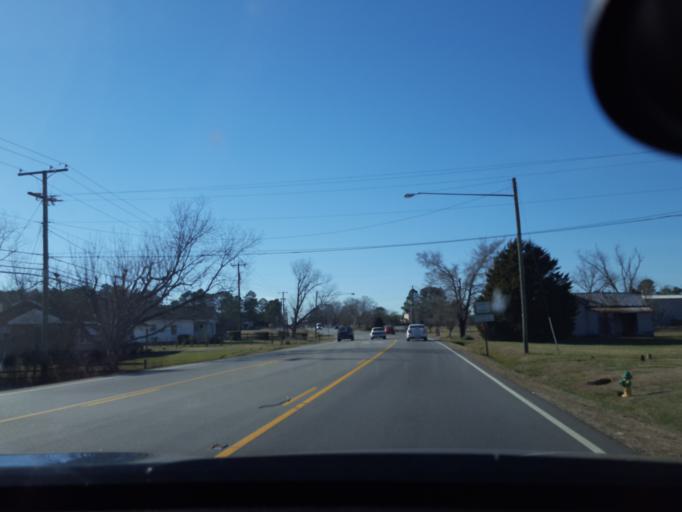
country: US
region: North Carolina
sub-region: Halifax County
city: South Rosemary
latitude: 36.4429
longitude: -77.6736
